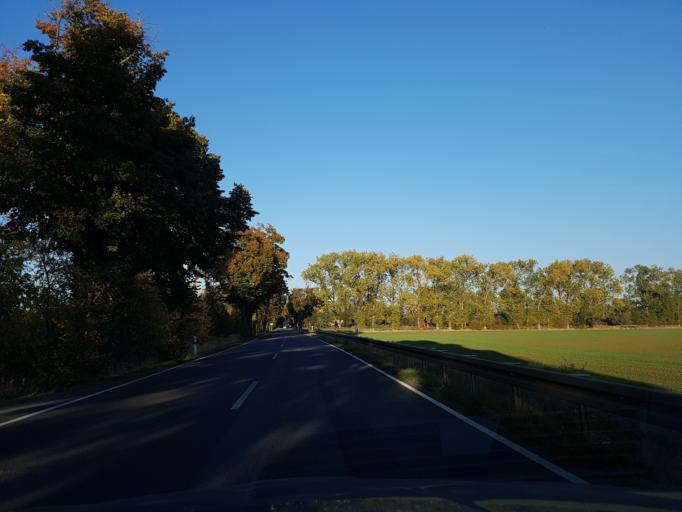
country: DE
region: Brandenburg
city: Bad Liebenwerda
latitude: 51.5138
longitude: 13.3781
